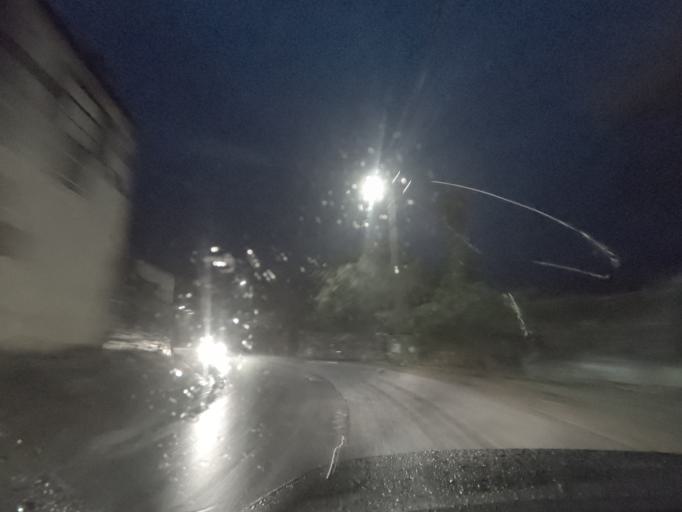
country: PT
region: Vila Real
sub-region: Sabrosa
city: Sabrosa
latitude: 41.2470
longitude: -7.5768
